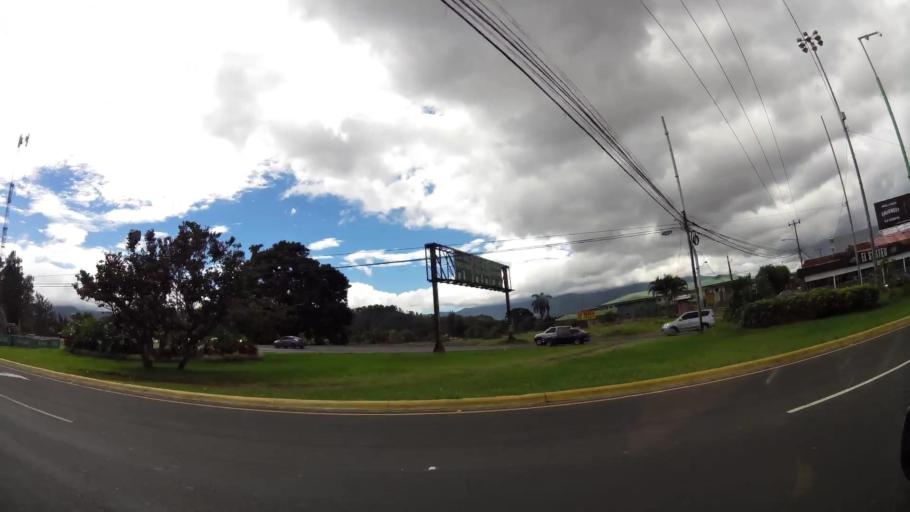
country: CR
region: San Jose
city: Curridabat
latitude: 9.9144
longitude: -84.0303
